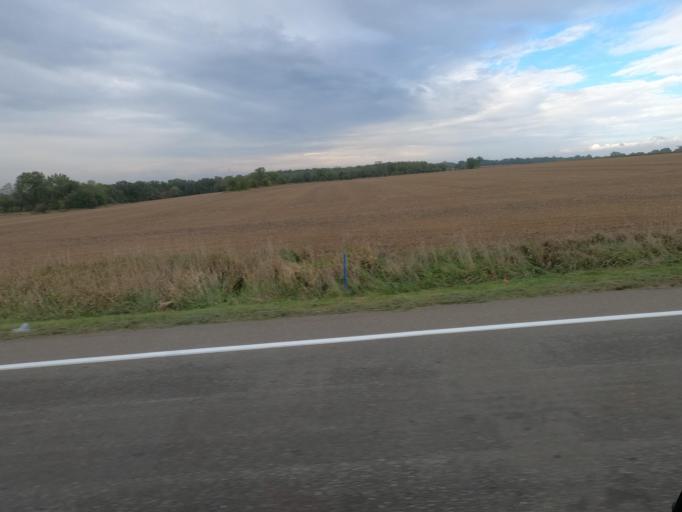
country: US
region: Iowa
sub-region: Henry County
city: Mount Pleasant
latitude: 40.7846
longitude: -91.6718
